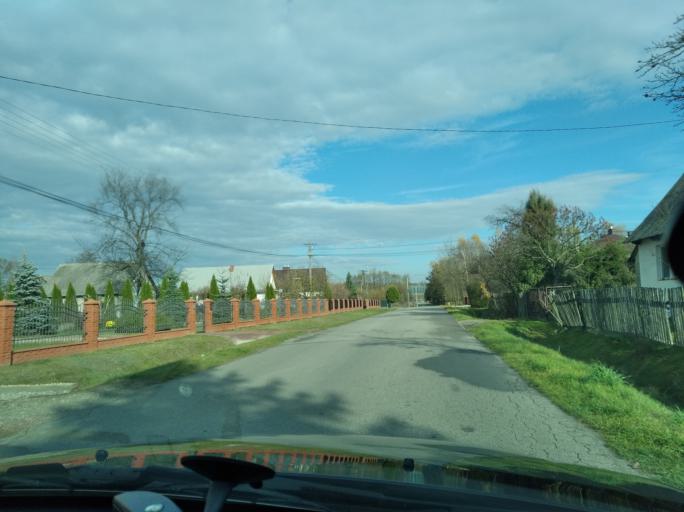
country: PL
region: Subcarpathian Voivodeship
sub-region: Powiat ropczycko-sedziszowski
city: Sedziszow Malopolski
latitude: 50.1064
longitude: 21.6843
